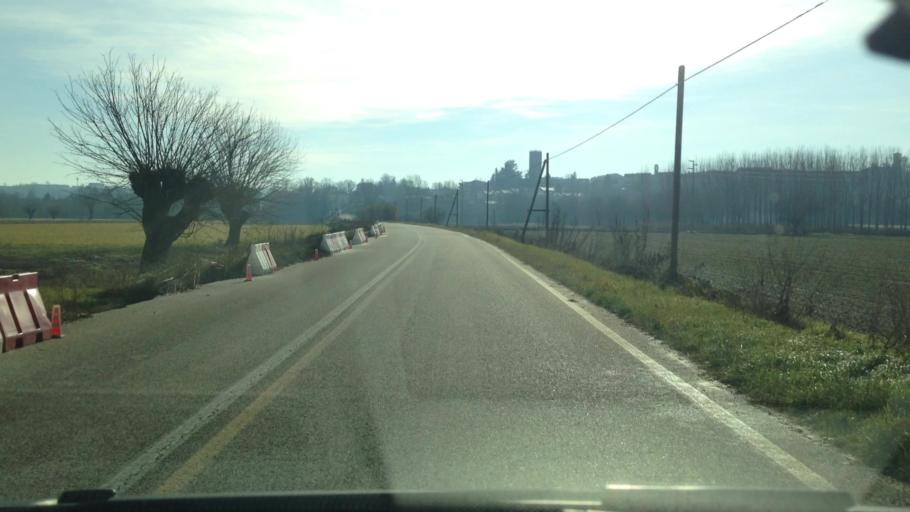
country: IT
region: Piedmont
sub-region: Provincia di Alessandria
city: Masio
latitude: 44.8773
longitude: 8.4094
